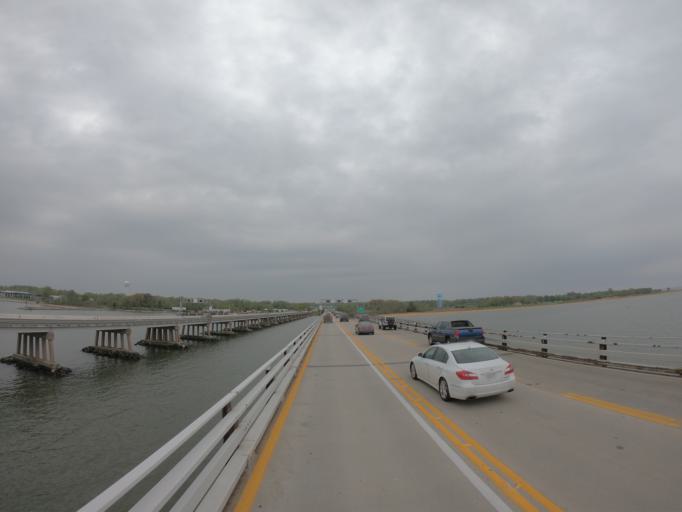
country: US
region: Maryland
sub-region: Anne Arundel County
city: Cape Saint Claire
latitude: 39.0054
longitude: -76.4015
